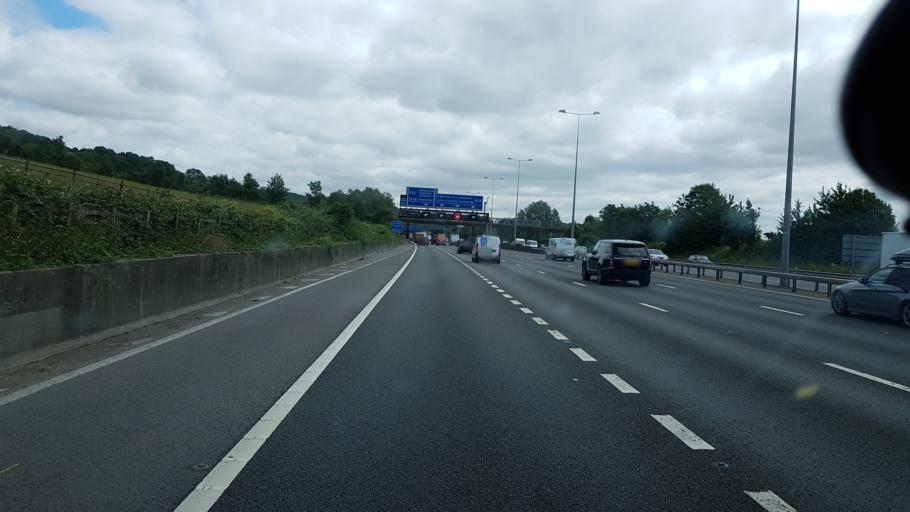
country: GB
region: England
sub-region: Surrey
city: Godstone
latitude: 51.2577
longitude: -0.0817
